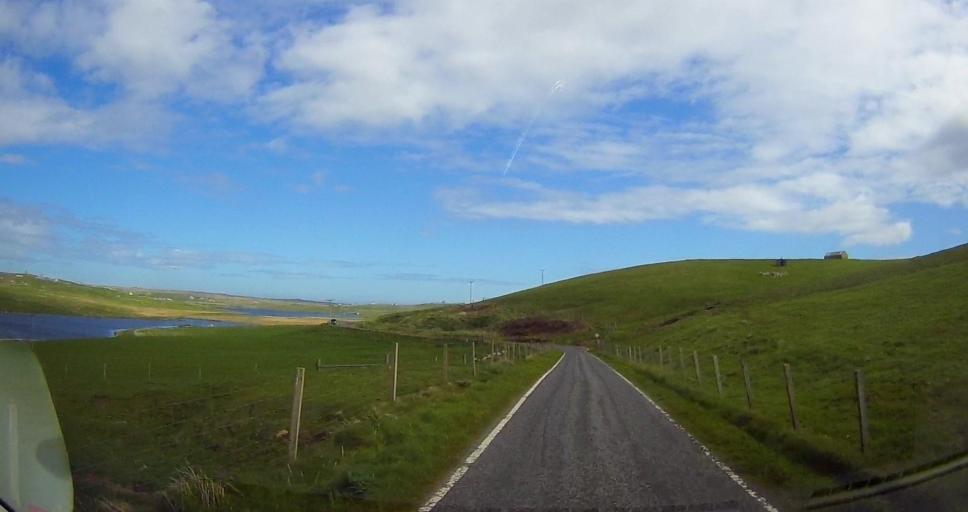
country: GB
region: Scotland
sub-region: Shetland Islands
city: Sandwick
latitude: 59.9248
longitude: -1.3397
